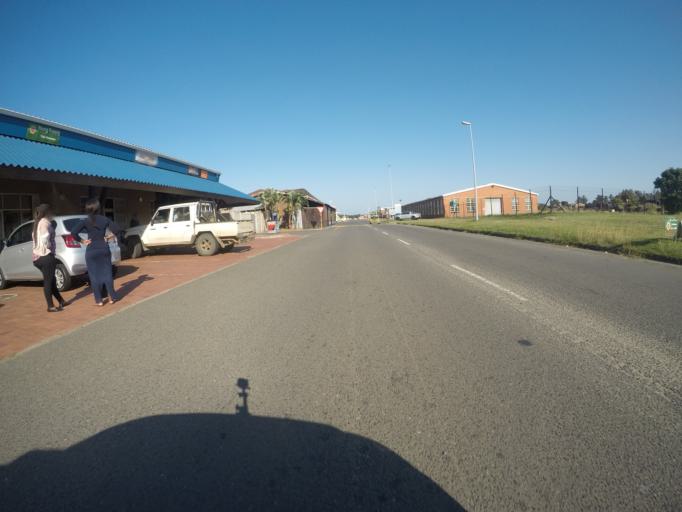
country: ZA
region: KwaZulu-Natal
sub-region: uThungulu District Municipality
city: Richards Bay
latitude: -28.7927
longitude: 32.0776
